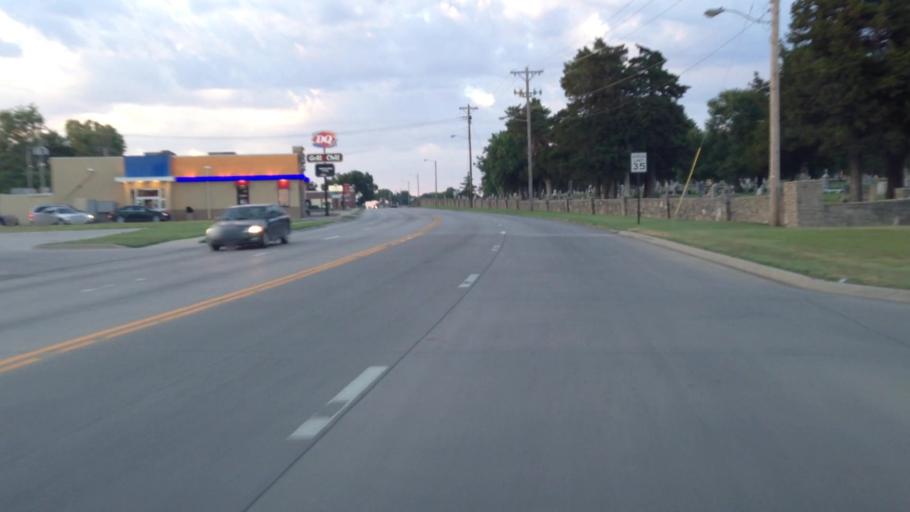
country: US
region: Kansas
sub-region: Montgomery County
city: Independence
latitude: 37.2364
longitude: -95.7063
